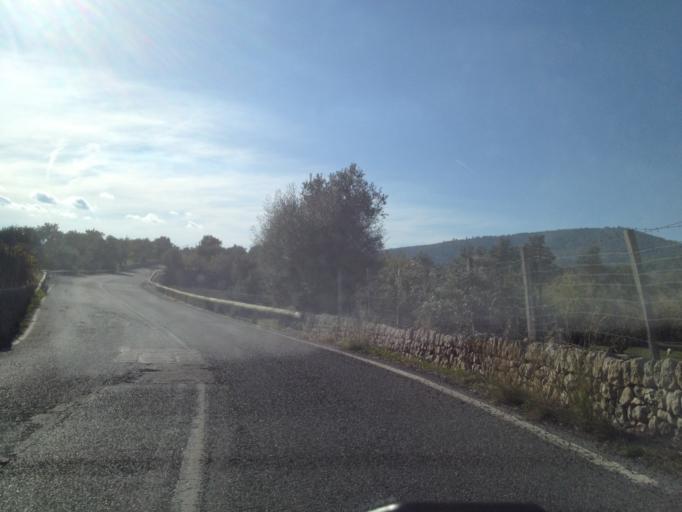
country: ES
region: Balearic Islands
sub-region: Illes Balears
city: Selva
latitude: 39.7408
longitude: 2.8907
